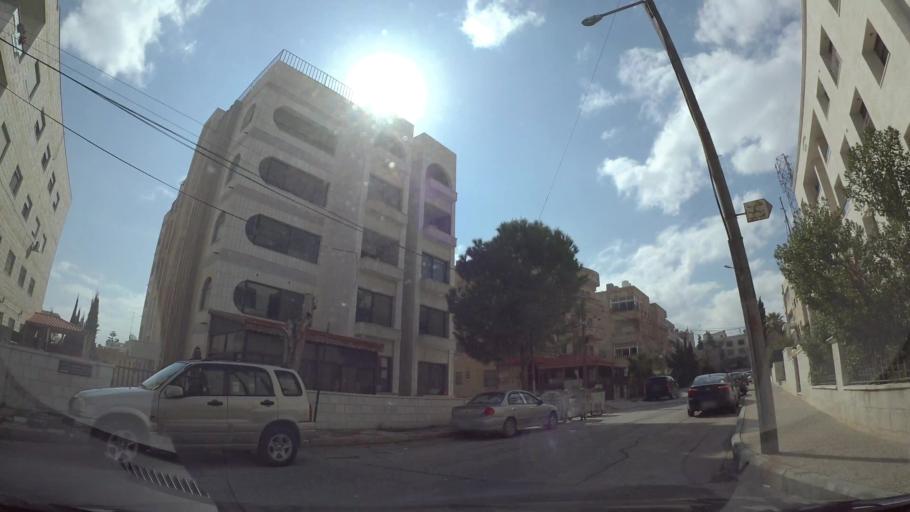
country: JO
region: Amman
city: Amman
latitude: 31.9727
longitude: 35.8934
